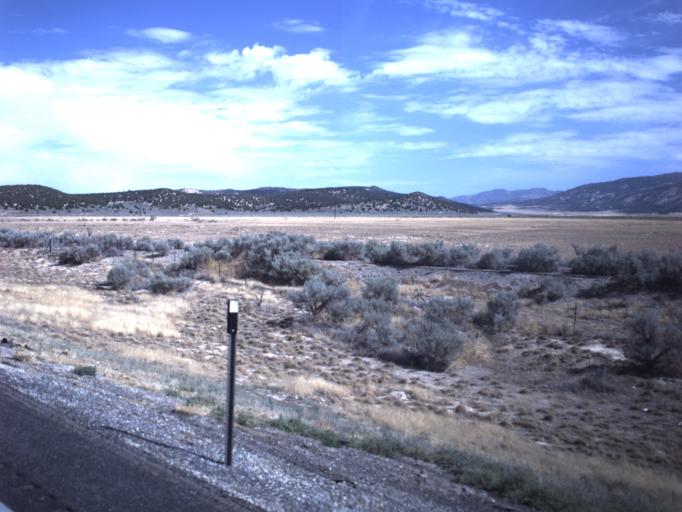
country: US
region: Utah
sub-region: Sanpete County
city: Gunnison
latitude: 39.3152
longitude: -111.9034
